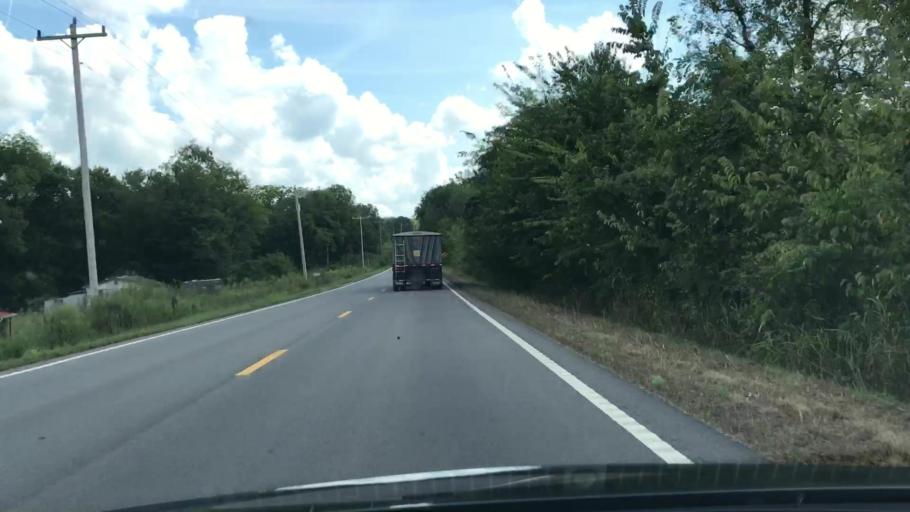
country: US
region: Tennessee
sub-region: Robertson County
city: Springfield
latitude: 36.6312
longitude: -86.9620
